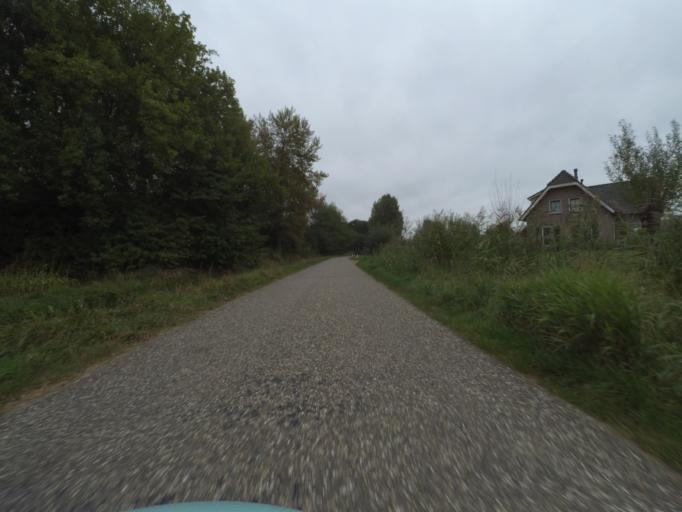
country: NL
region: Gelderland
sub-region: Gemeente Tiel
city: Tiel
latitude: 51.9066
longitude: 5.3905
